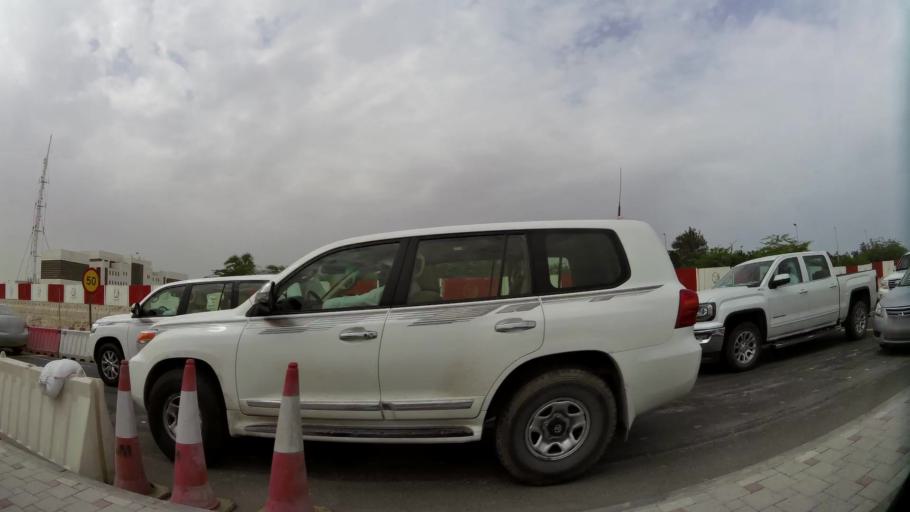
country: QA
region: Baladiyat ar Rayyan
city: Ar Rayyan
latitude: 25.3530
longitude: 51.4596
